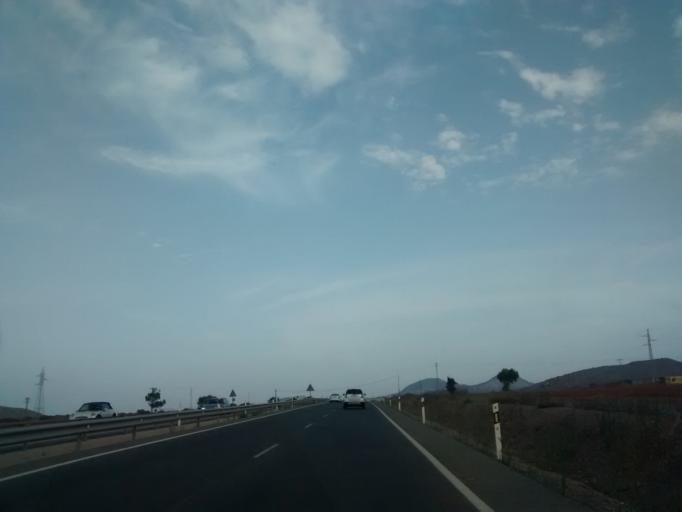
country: ES
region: Murcia
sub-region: Murcia
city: La Union
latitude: 37.6389
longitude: -0.8186
